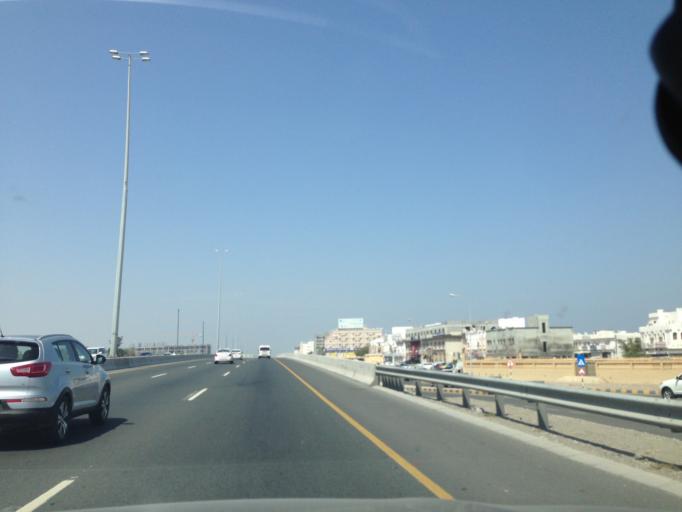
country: OM
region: Muhafazat Masqat
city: As Sib al Jadidah
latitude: 23.6340
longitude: 58.2301
